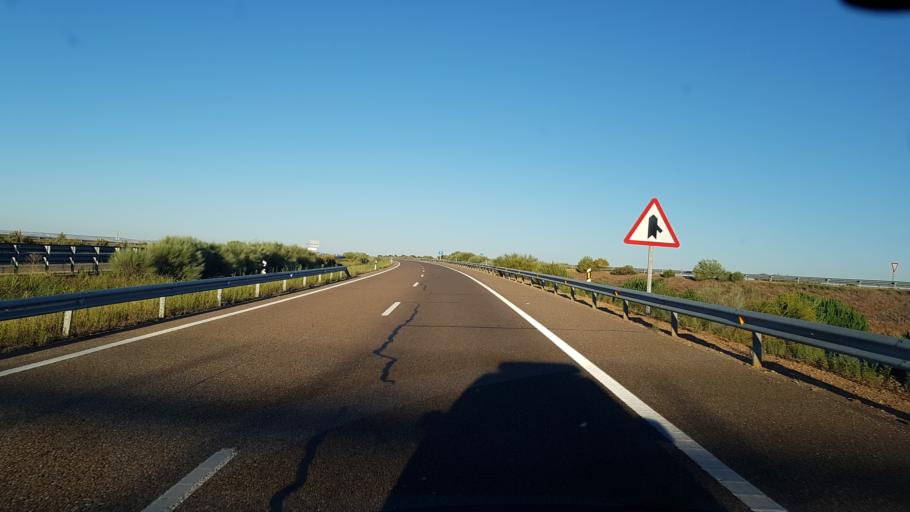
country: ES
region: Castille and Leon
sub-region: Provincia de Zamora
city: Matilla la Seca
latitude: 41.5648
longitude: -5.5228
